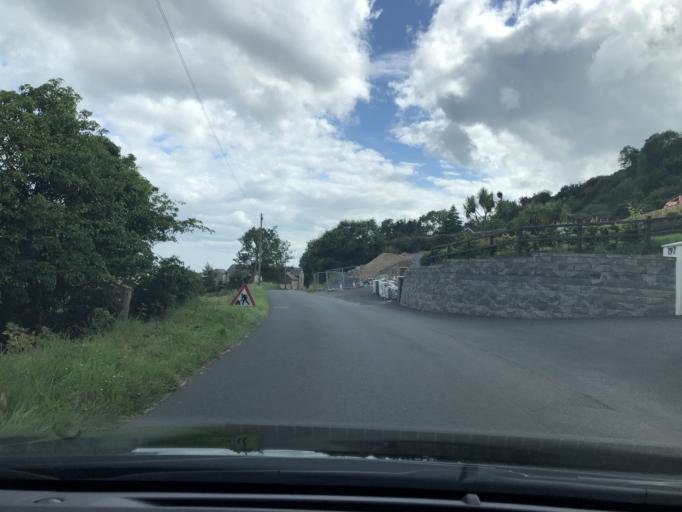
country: GB
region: Northern Ireland
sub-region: Ards District
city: Newtownards
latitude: 54.5811
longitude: -5.7113
